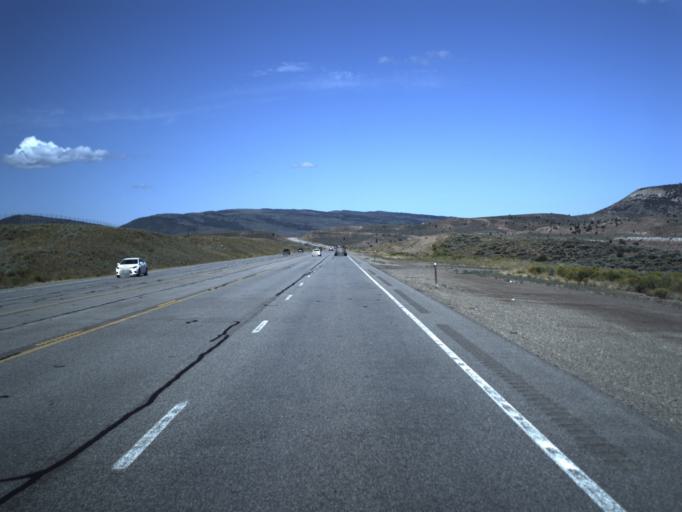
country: US
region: Utah
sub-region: Carbon County
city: Helper
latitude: 39.8350
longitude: -110.9746
